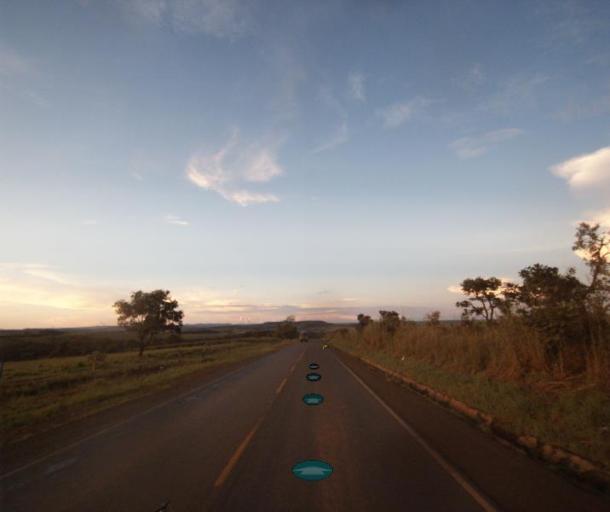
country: BR
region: Goias
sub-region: Pirenopolis
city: Pirenopolis
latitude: -16.0014
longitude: -48.8404
